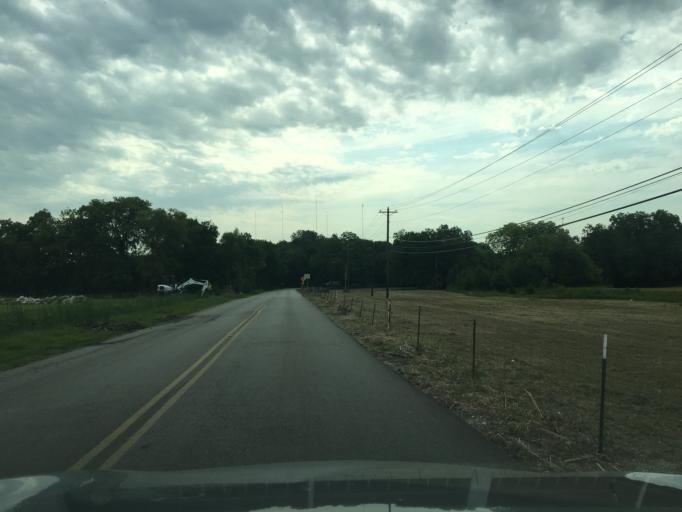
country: US
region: Texas
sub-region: Collin County
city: Saint Paul
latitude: 33.0331
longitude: -96.5834
